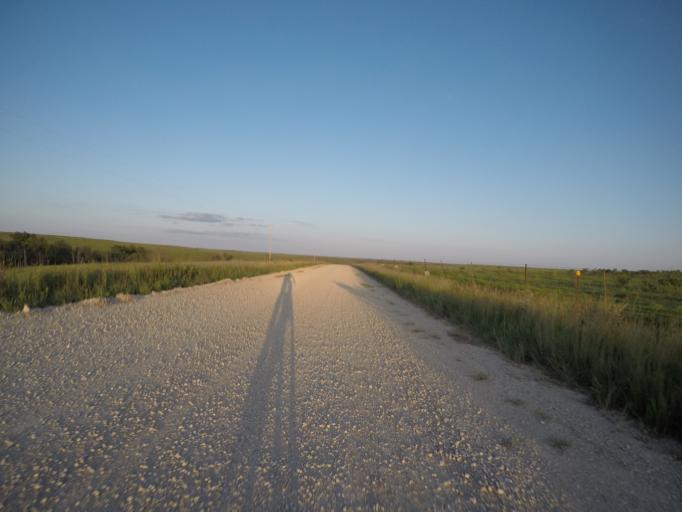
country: US
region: Kansas
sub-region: Riley County
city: Ogden
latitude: 39.0070
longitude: -96.6273
